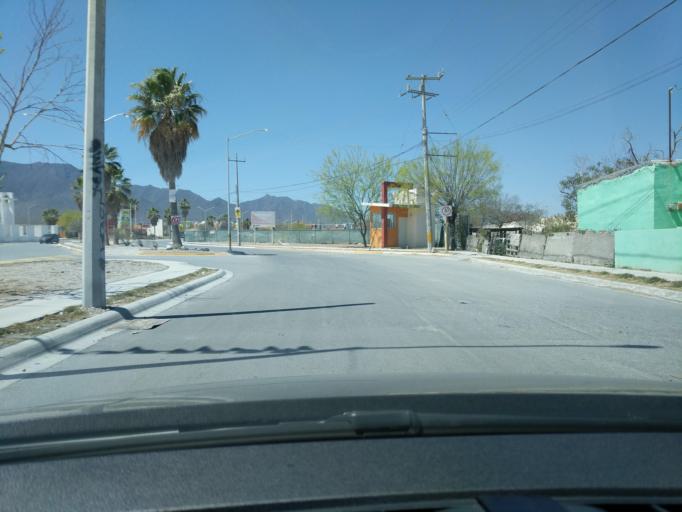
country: MX
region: Nuevo Leon
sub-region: Salinas Victoria
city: Las Torres
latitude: 25.9623
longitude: -100.3034
